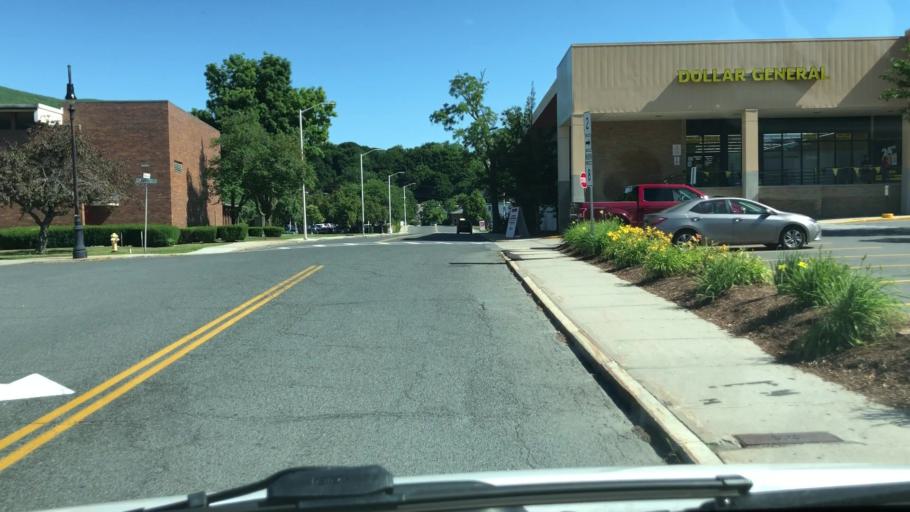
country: US
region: Massachusetts
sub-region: Berkshire County
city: North Adams
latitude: 42.7006
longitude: -73.1119
